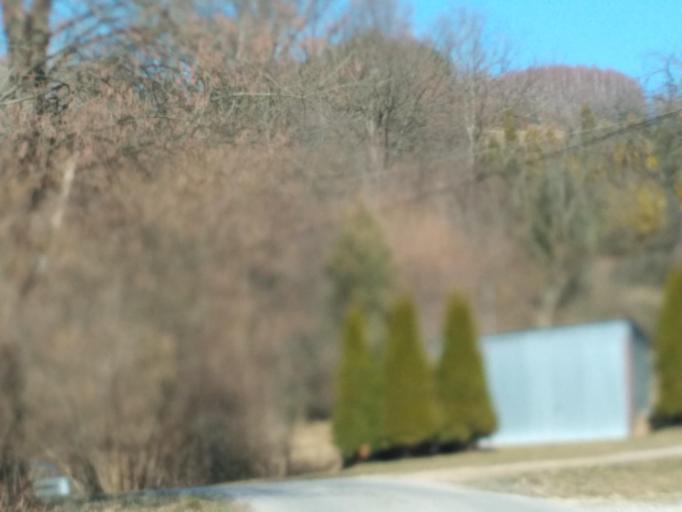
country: PL
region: Subcarpathian Voivodeship
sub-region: Powiat ropczycko-sedziszowski
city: Iwierzyce
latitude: 49.9513
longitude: 21.7495
